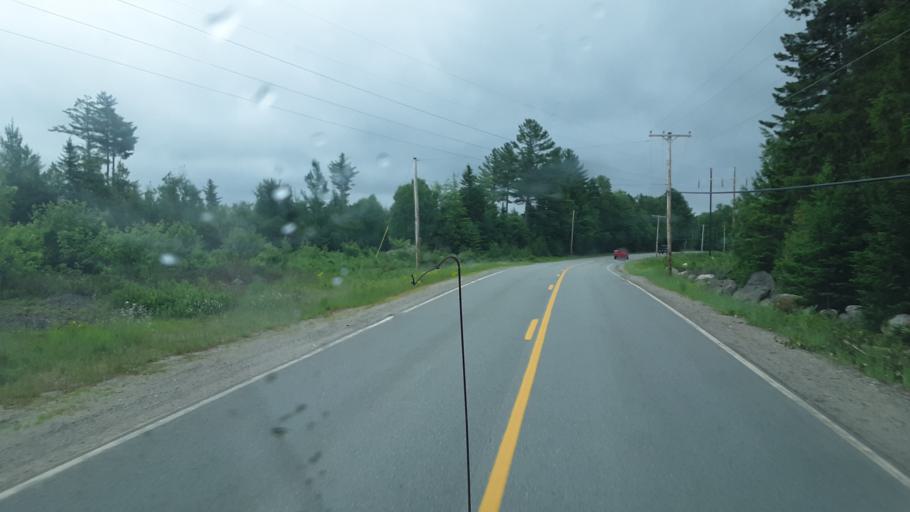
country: US
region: Maine
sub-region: Penobscot County
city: Millinocket
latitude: 45.6811
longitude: -68.7619
